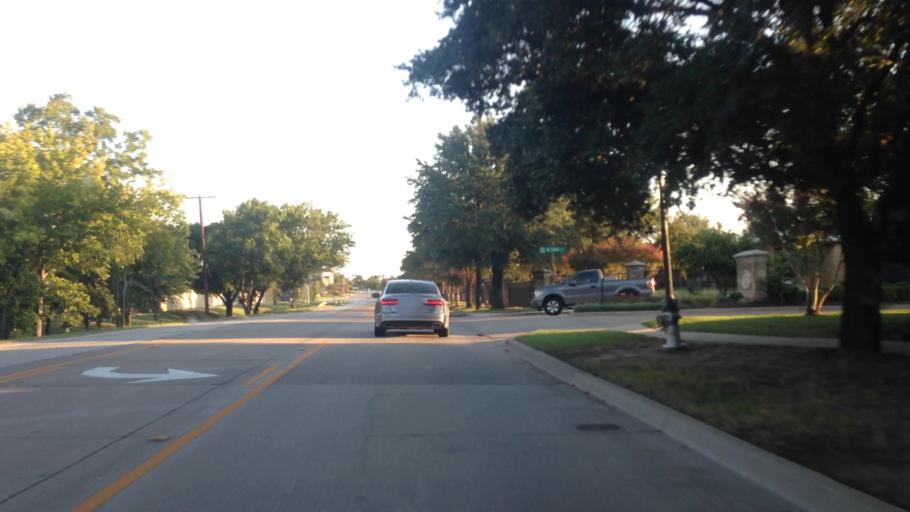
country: US
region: Texas
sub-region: Tarrant County
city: Southlake
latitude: 32.9362
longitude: -97.1336
